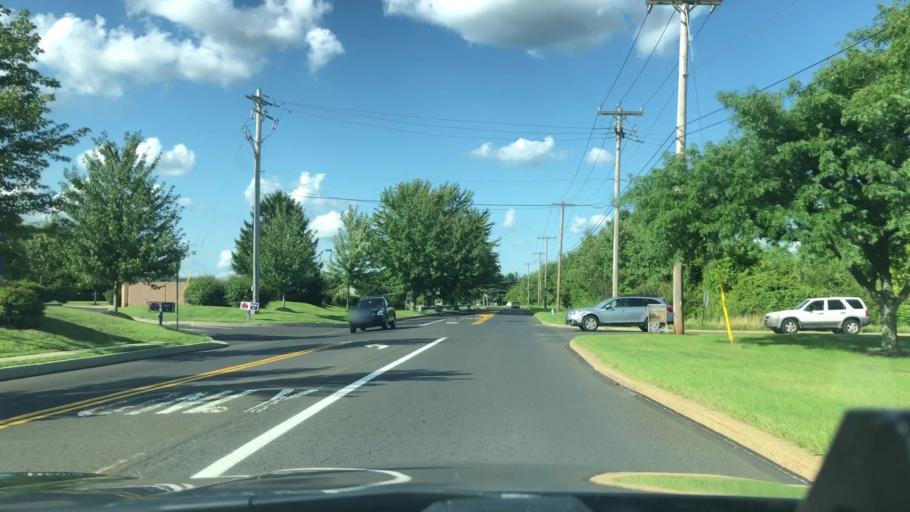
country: US
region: Pennsylvania
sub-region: Montgomery County
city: Montgomeryville
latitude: 40.2423
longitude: -75.2417
